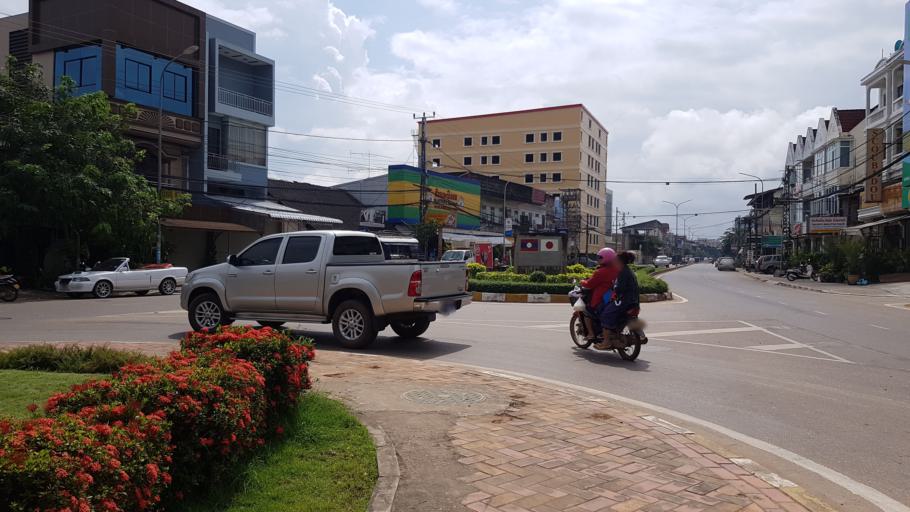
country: LA
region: Vientiane
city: Vientiane
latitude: 17.9570
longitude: 102.6177
